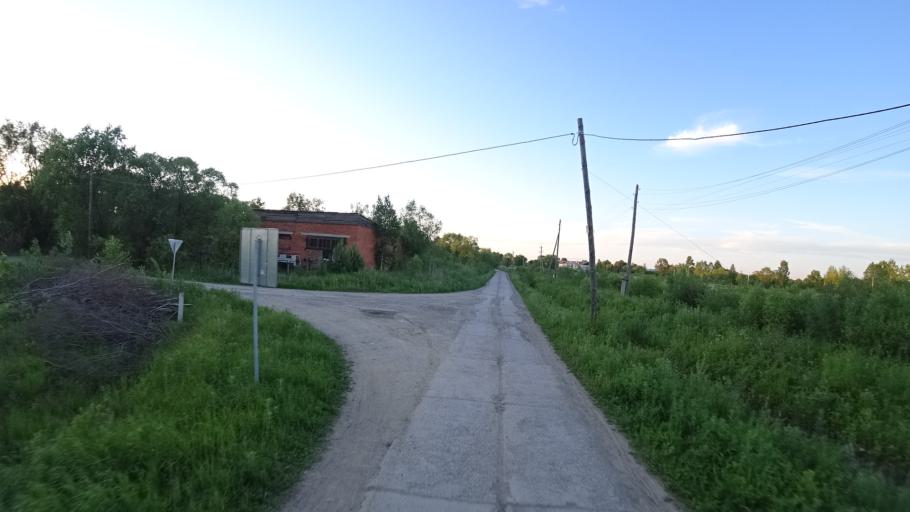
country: RU
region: Khabarovsk Krai
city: Khor
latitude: 47.8485
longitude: 134.9561
